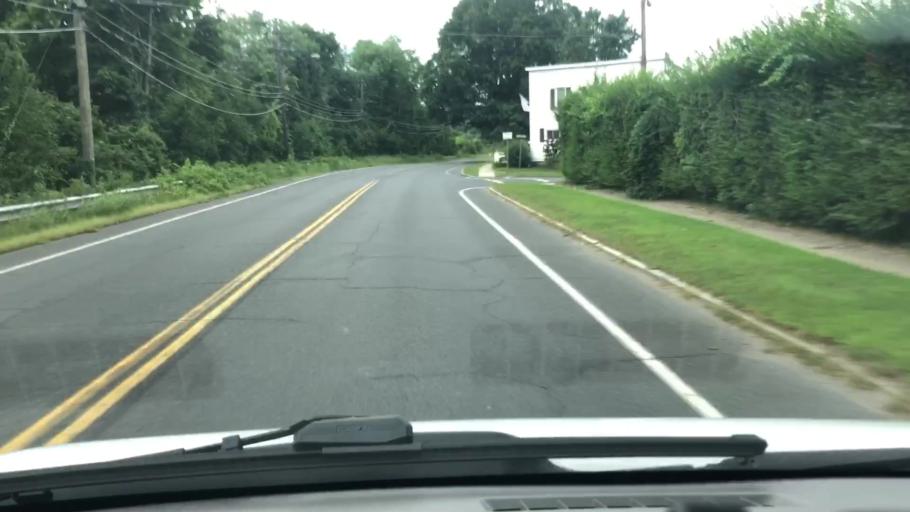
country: US
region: Massachusetts
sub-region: Franklin County
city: Turners Falls
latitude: 42.5987
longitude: -72.5644
